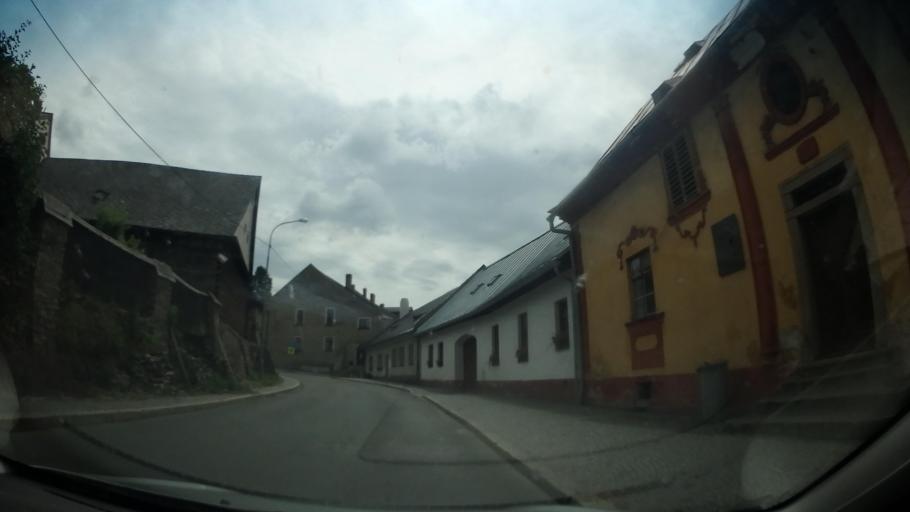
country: CZ
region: Vysocina
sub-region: Okres Zd'ar nad Sazavou
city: Nove Mesto na Morave
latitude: 49.5607
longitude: 16.0718
